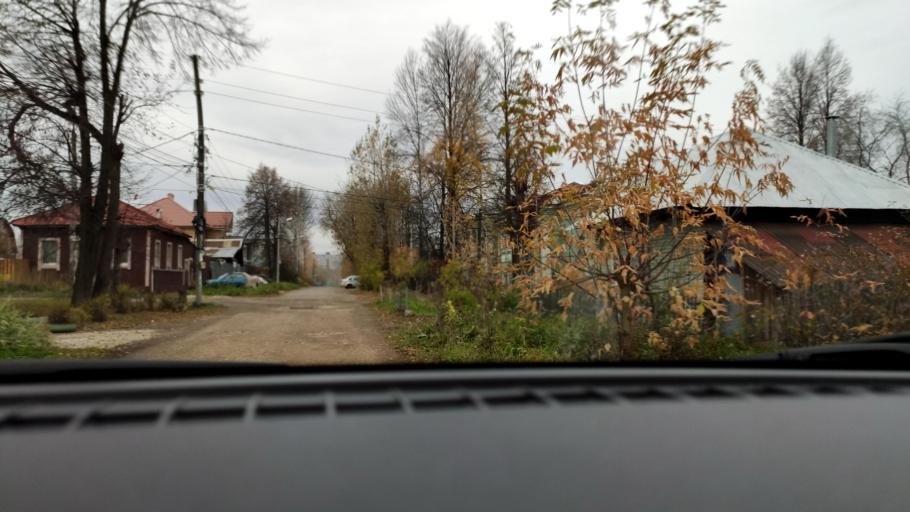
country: RU
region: Perm
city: Perm
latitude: 58.0225
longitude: 56.3181
